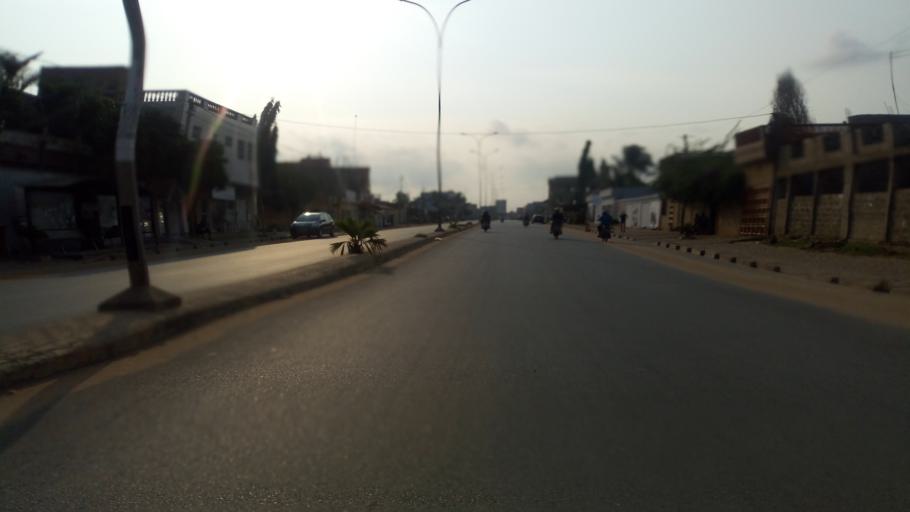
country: TG
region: Maritime
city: Lome
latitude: 6.1979
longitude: 1.1853
